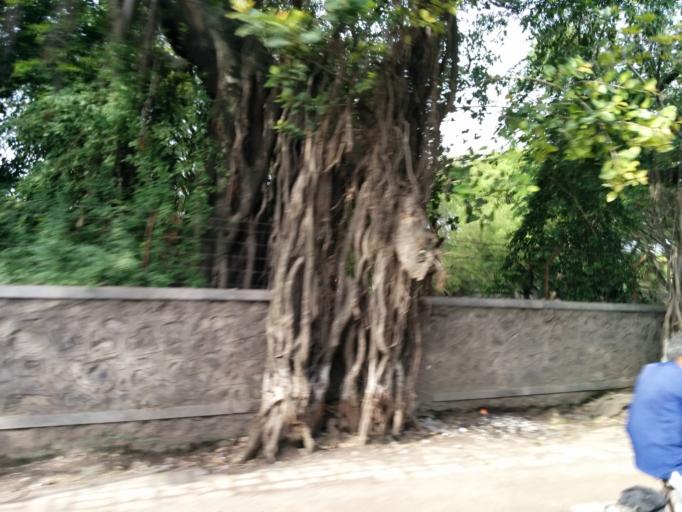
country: IN
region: Maharashtra
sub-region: Pune Division
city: Pune
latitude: 18.5066
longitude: 73.8853
